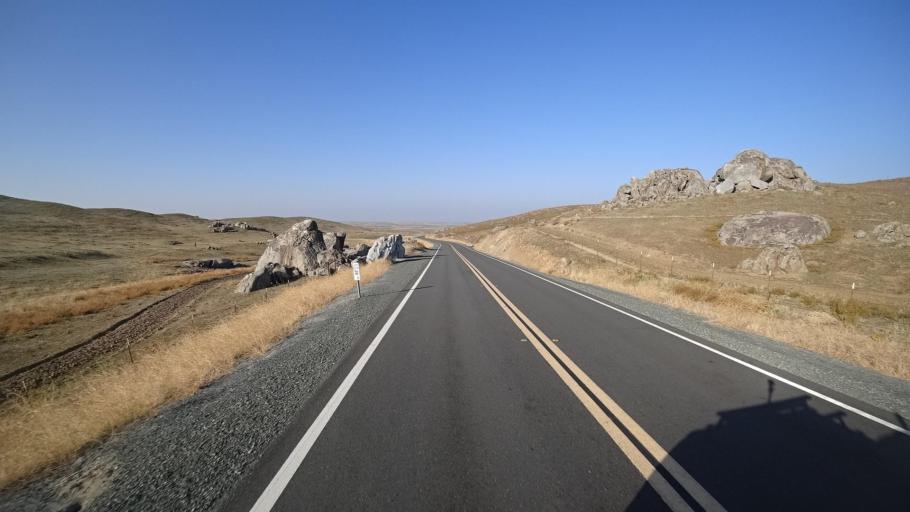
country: US
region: California
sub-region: Tulare County
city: Richgrove
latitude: 35.7422
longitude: -118.9063
